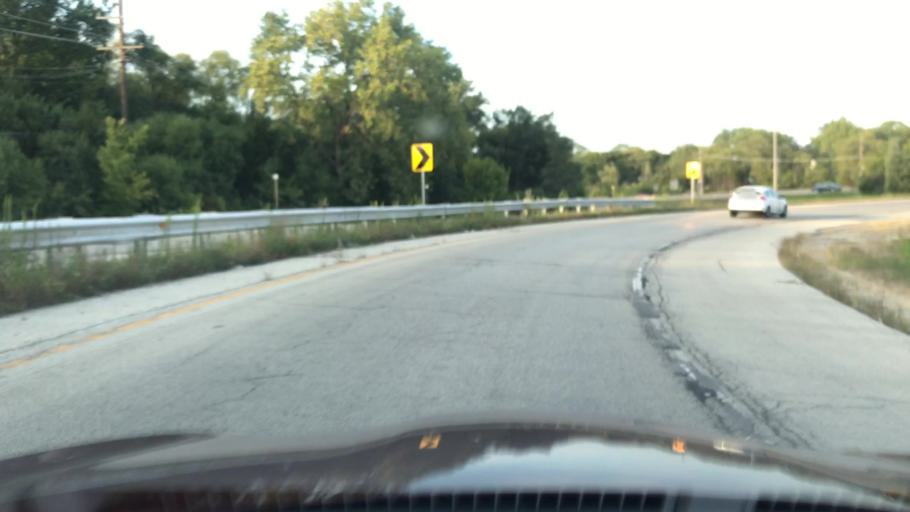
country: US
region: Illinois
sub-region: DuPage County
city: Oakbrook Terrace
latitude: 41.8622
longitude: -87.9609
